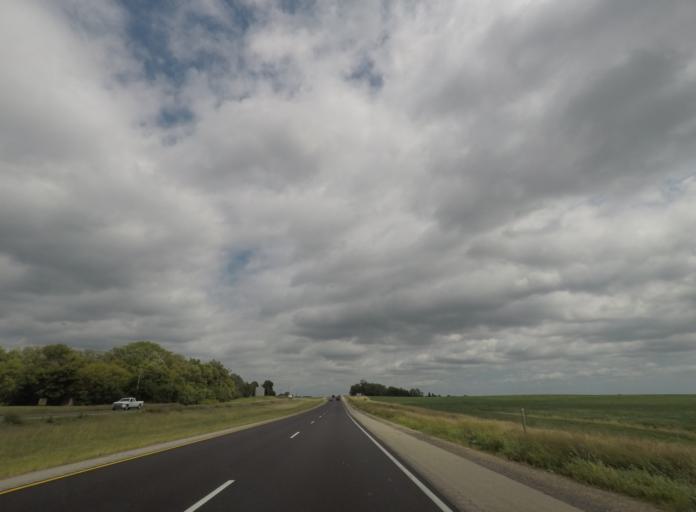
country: US
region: Iowa
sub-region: Linn County
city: Ely
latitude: 41.9264
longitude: -91.6289
